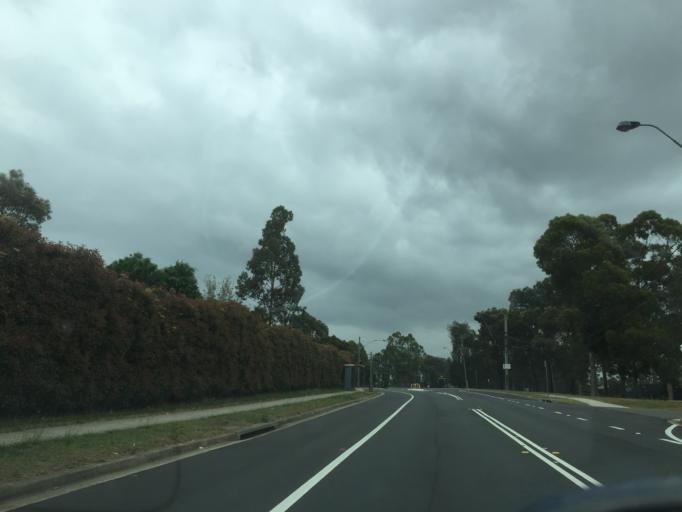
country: AU
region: New South Wales
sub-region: Blacktown
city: Blacktown
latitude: -33.7864
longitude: 150.8922
